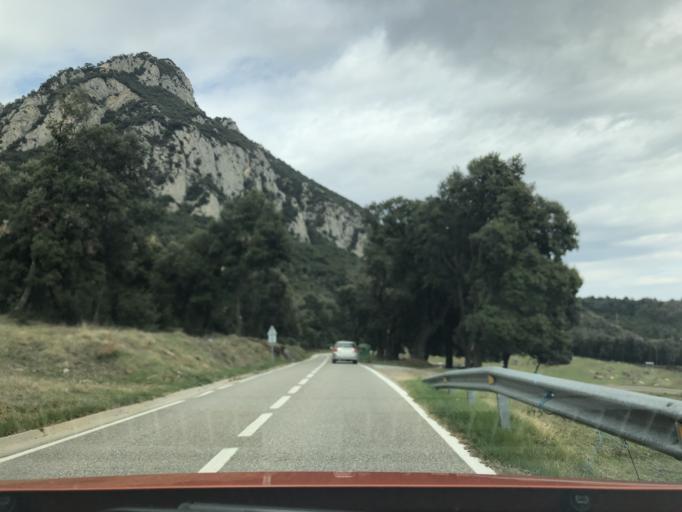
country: ES
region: Catalonia
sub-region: Provincia de Barcelona
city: Berga
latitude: 42.1018
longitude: 1.8161
